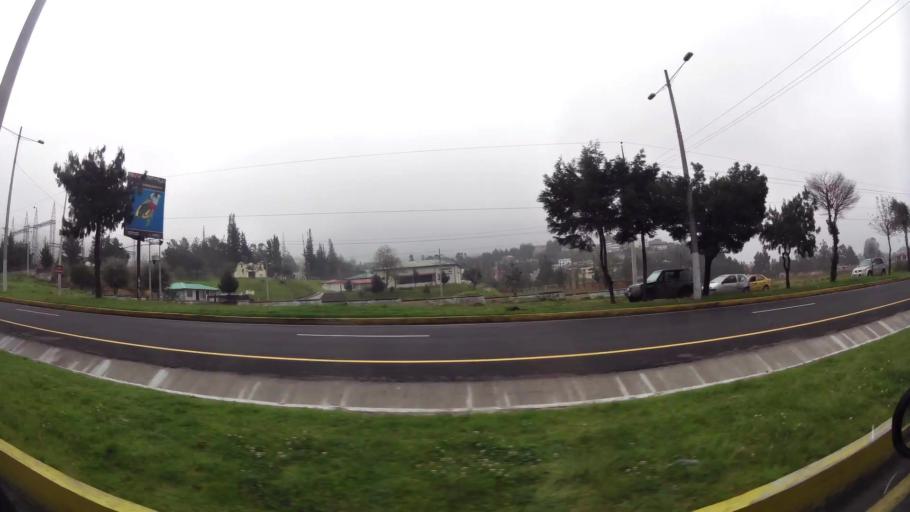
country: EC
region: Pichincha
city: Quito
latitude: -0.2765
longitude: -78.4879
